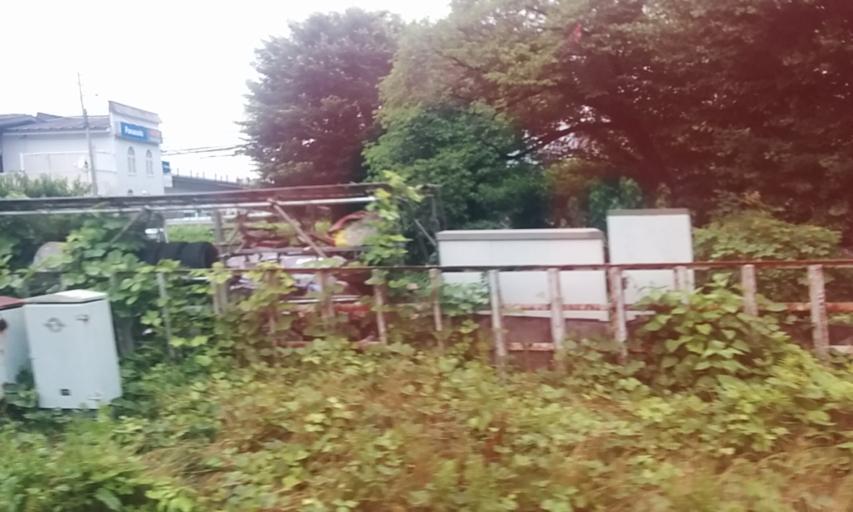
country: JP
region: Tokyo
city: Hino
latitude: 35.6639
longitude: 139.4075
